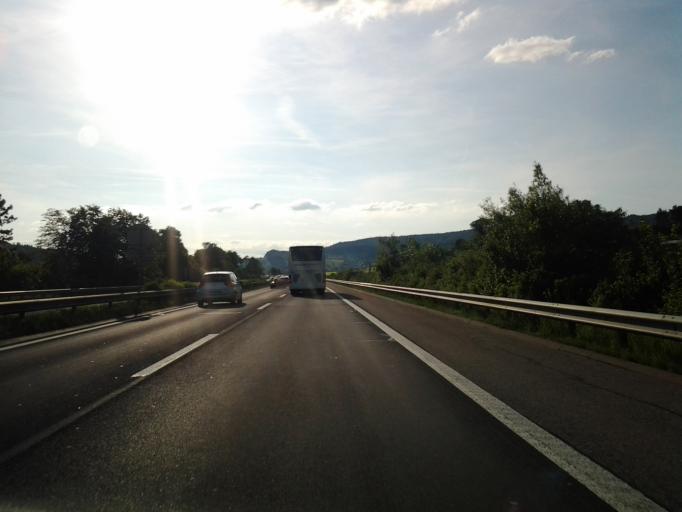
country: CH
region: Lucerne
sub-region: Sursee District
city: Knutwil
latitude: 47.2013
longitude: 8.0538
